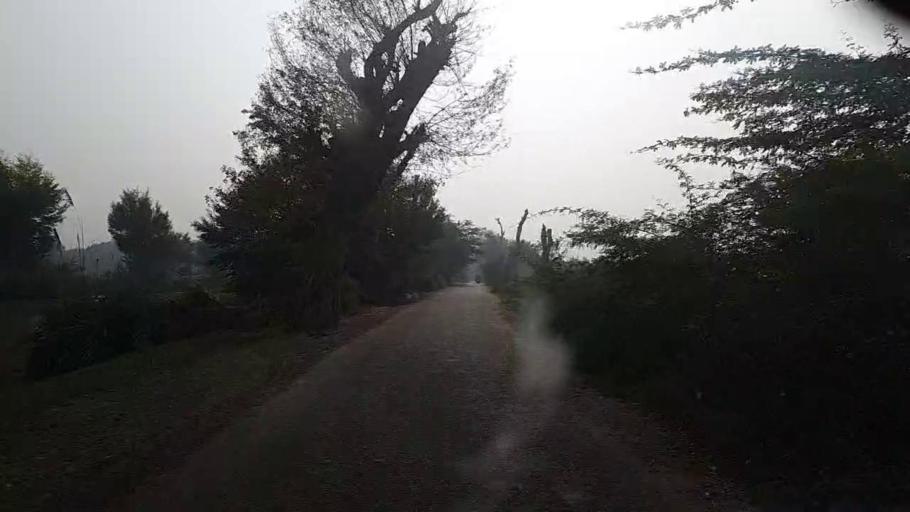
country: PK
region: Sindh
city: Bozdar
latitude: 27.1394
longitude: 68.6549
